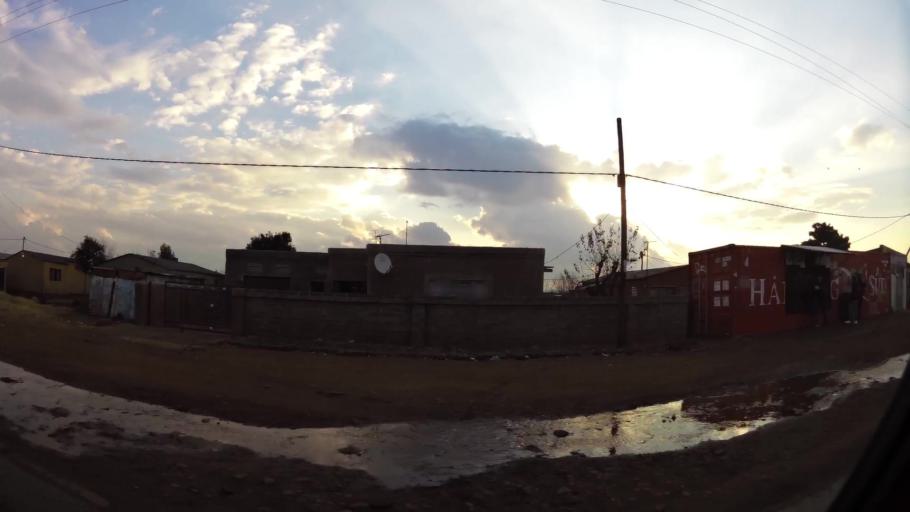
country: ZA
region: Gauteng
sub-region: City of Johannesburg Metropolitan Municipality
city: Orange Farm
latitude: -26.5482
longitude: 27.8333
